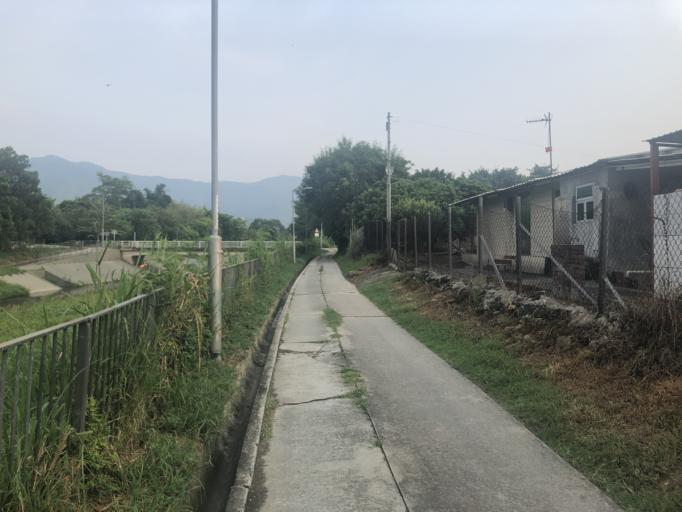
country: CN
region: Guangdong
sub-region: Shenzhen
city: Shenzhen
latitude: 22.4862
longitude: 114.1025
